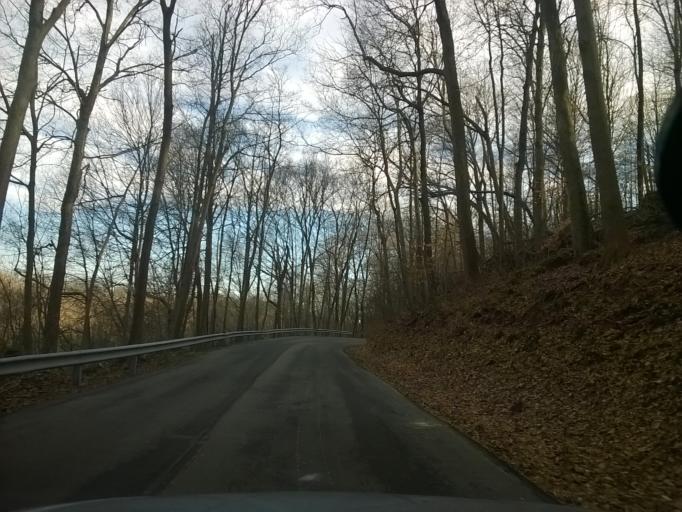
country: US
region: Indiana
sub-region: Jefferson County
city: Hanover
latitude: 38.7214
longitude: -85.4601
